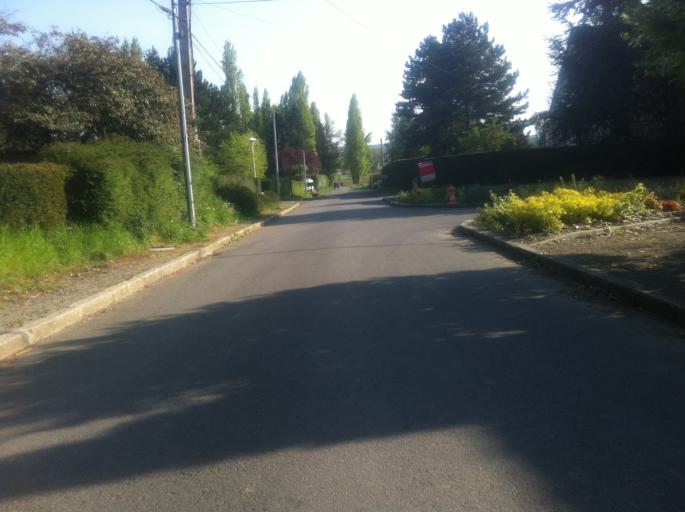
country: FR
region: Brittany
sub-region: Departement d'Ille-et-Vilaine
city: Bruz
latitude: 48.0205
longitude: -1.7293
